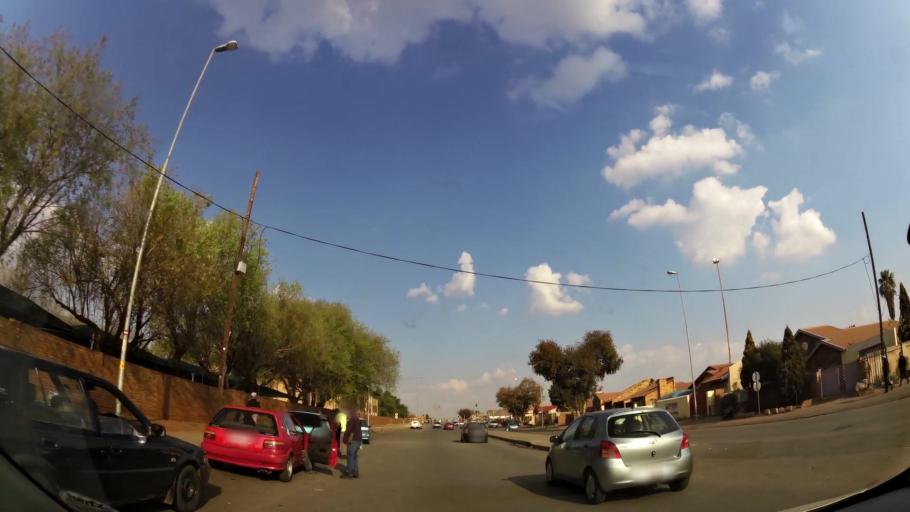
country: ZA
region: Gauteng
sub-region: Ekurhuleni Metropolitan Municipality
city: Germiston
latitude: -26.3442
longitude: 28.2170
